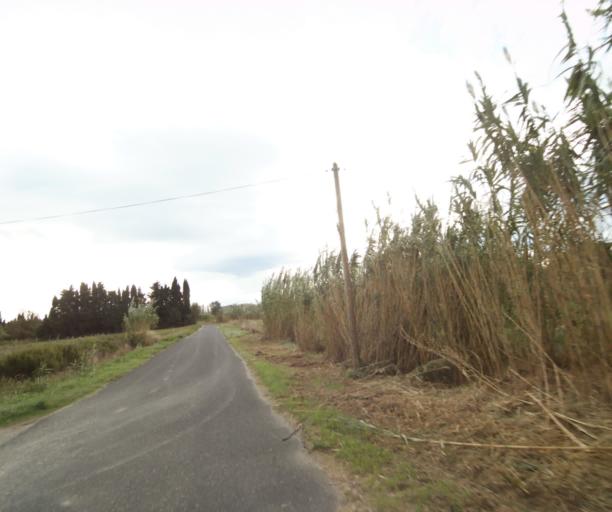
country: FR
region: Languedoc-Roussillon
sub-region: Departement des Pyrenees-Orientales
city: Argelers
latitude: 42.5783
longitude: 3.0203
